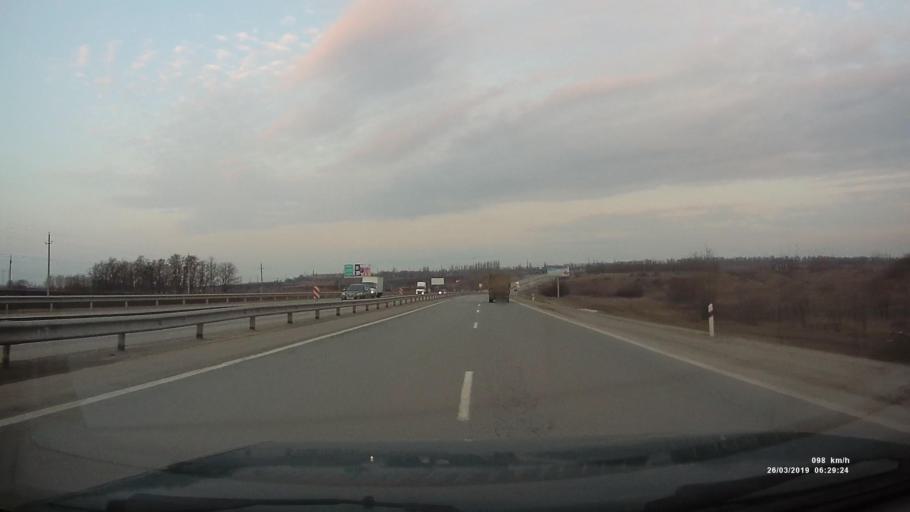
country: RU
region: Rostov
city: Kalinin
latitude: 47.2673
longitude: 39.5738
